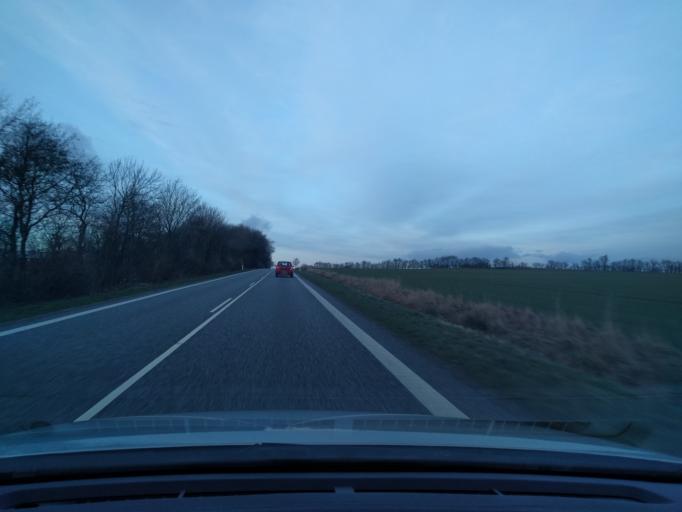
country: DK
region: South Denmark
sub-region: Tonder Kommune
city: Toftlund
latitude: 55.1499
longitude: 9.0252
